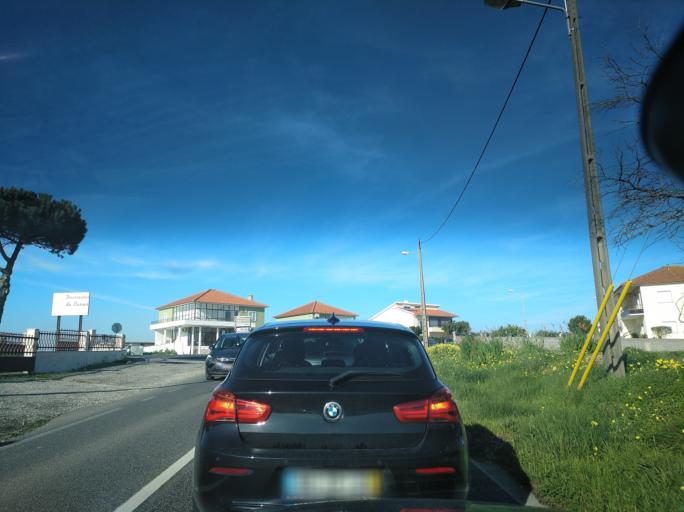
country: PT
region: Lisbon
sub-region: Mafra
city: Mafra
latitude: 38.9136
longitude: -9.3271
